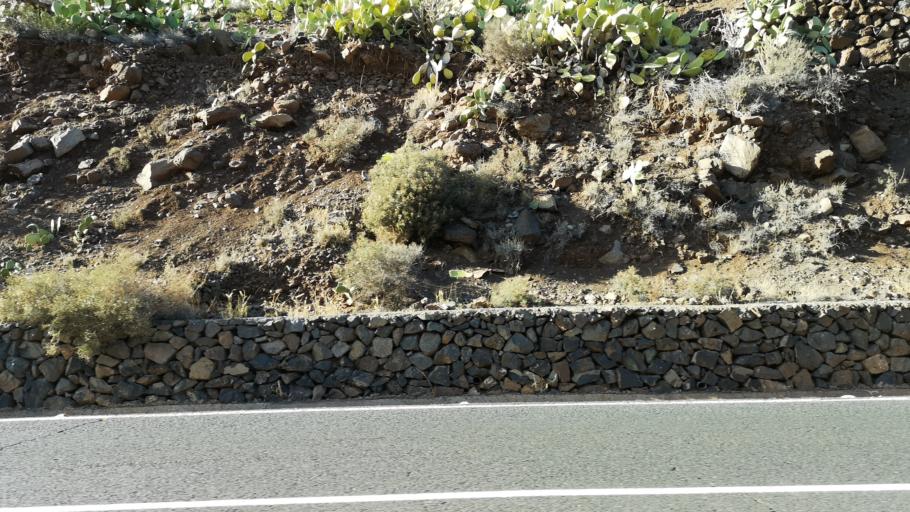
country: ES
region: Canary Islands
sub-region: Provincia de Santa Cruz de Tenerife
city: Vallehermosa
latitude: 28.1098
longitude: -17.3219
